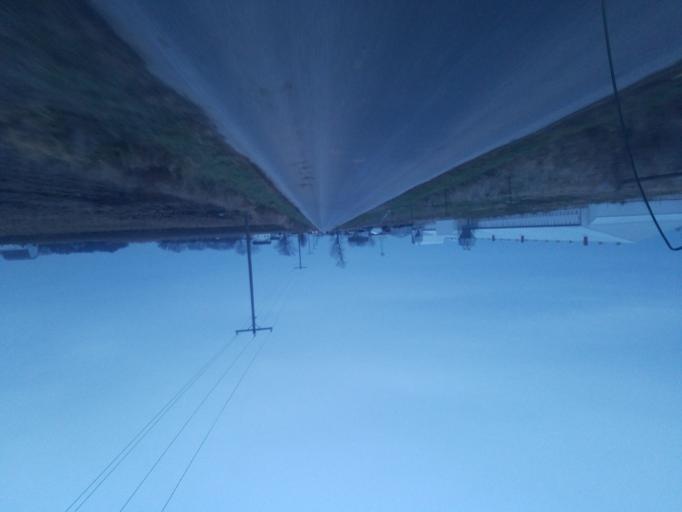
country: US
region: Indiana
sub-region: Adams County
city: Berne
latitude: 40.7313
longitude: -84.9081
